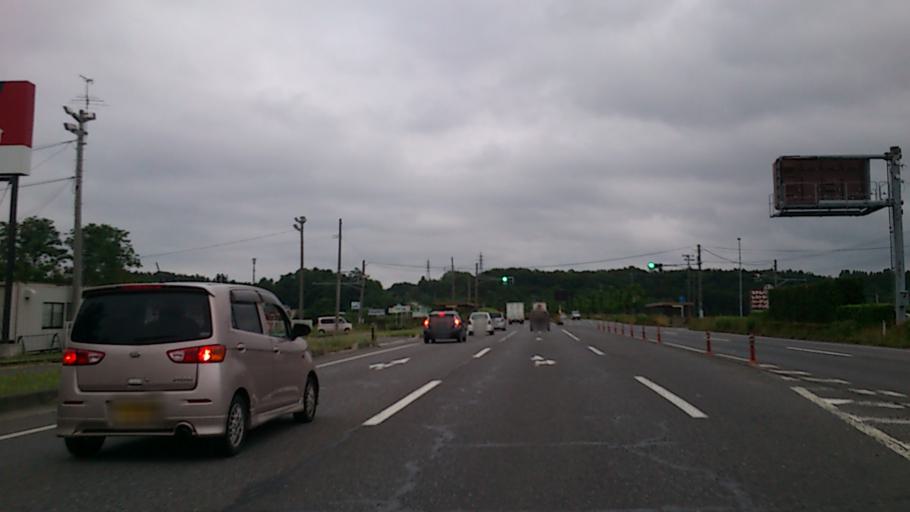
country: JP
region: Fukushima
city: Koriyama
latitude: 37.3647
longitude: 140.3492
